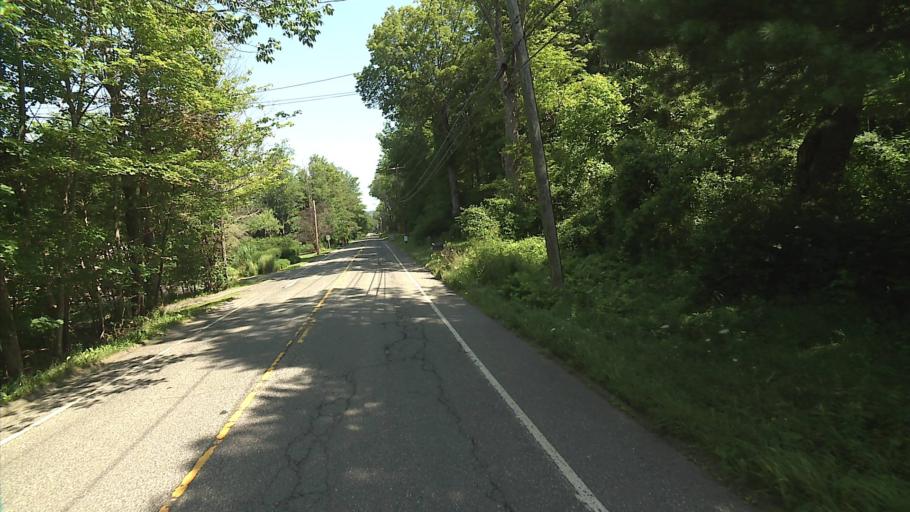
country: US
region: Connecticut
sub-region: Litchfield County
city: Winchester Center
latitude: 41.9770
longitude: -73.2005
